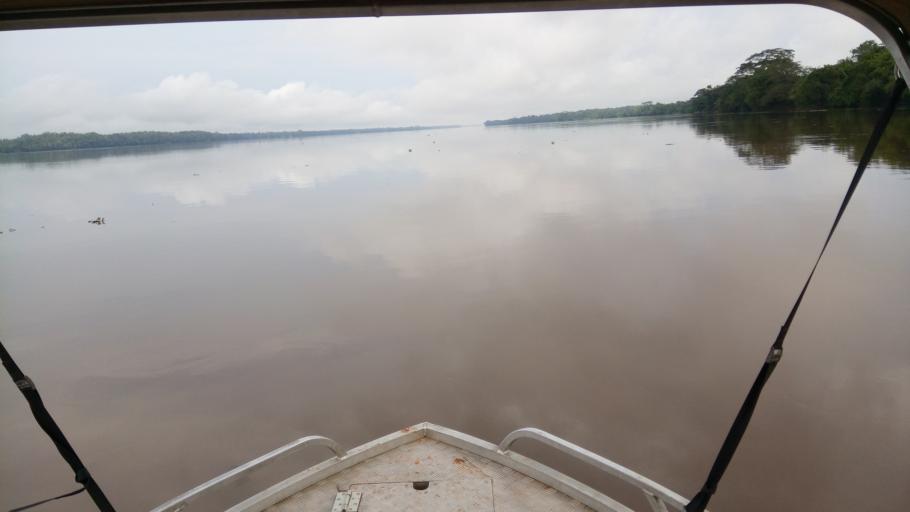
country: CD
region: Eastern Province
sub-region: Sous-Region de la Tshopo
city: Yangambi
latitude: 0.6359
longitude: 24.6776
